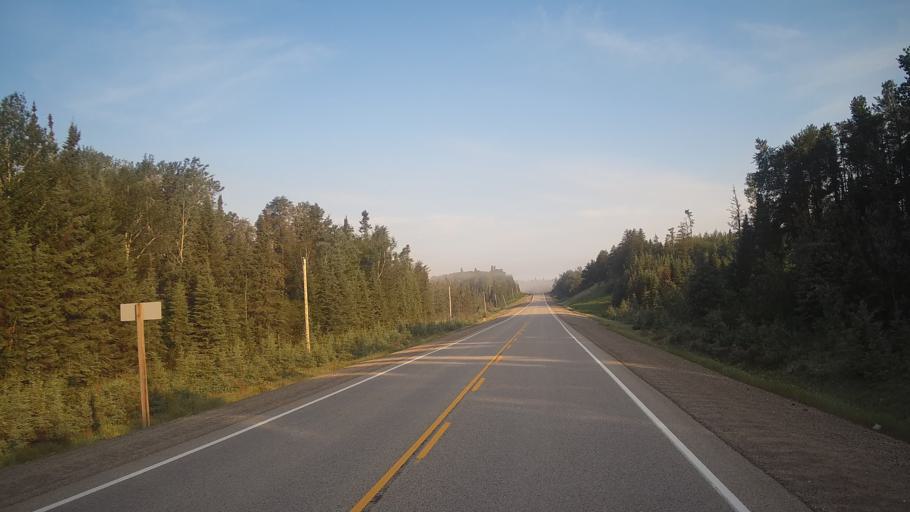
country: CA
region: Ontario
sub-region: Rainy River District
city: Atikokan
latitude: 49.3146
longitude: -91.3816
